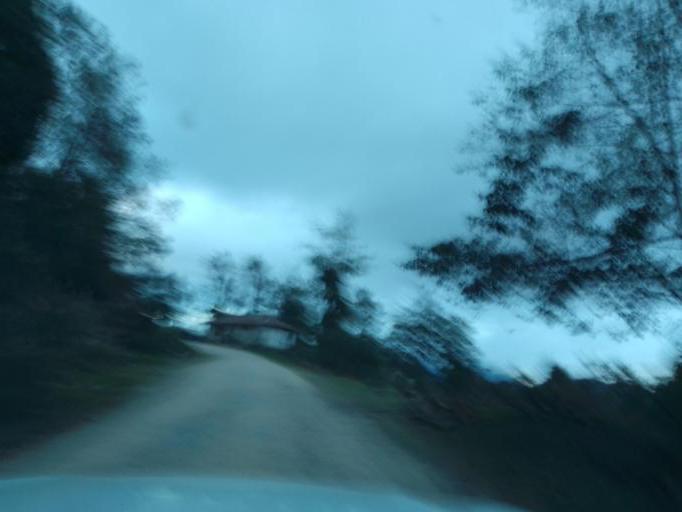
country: MX
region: Chiapas
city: Motozintla de Mendoza
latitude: 15.2196
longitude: -92.2379
